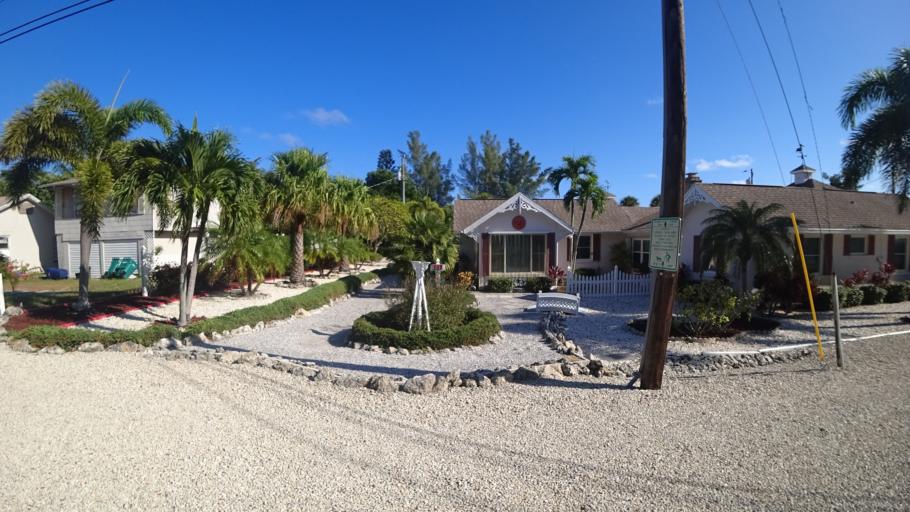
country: US
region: Florida
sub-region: Manatee County
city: Anna Maria
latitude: 27.5302
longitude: -82.7398
